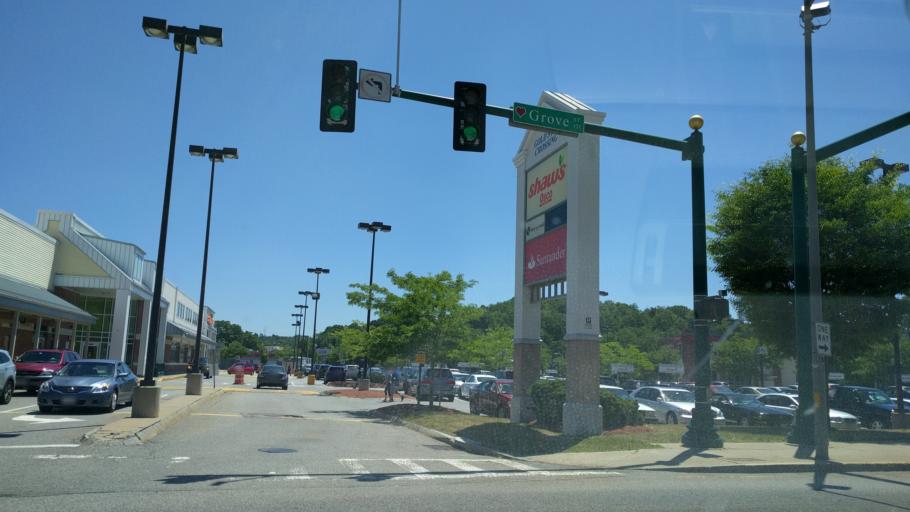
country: US
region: Massachusetts
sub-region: Worcester County
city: Worcester
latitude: 42.2884
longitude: -71.8075
